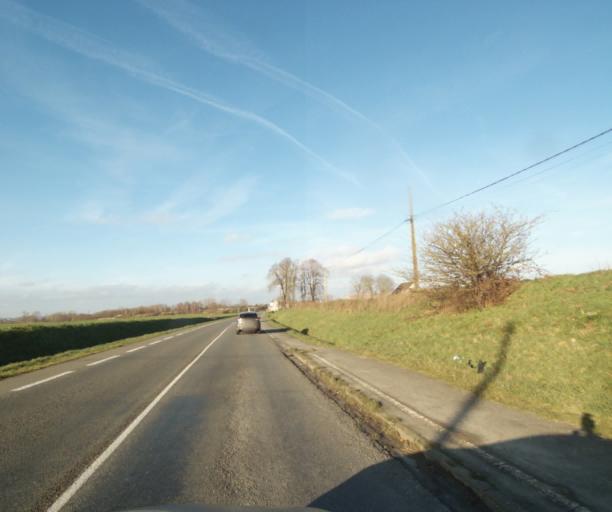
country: FR
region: Nord-Pas-de-Calais
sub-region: Departement du Nord
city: Marly
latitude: 50.3291
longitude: 3.5592
